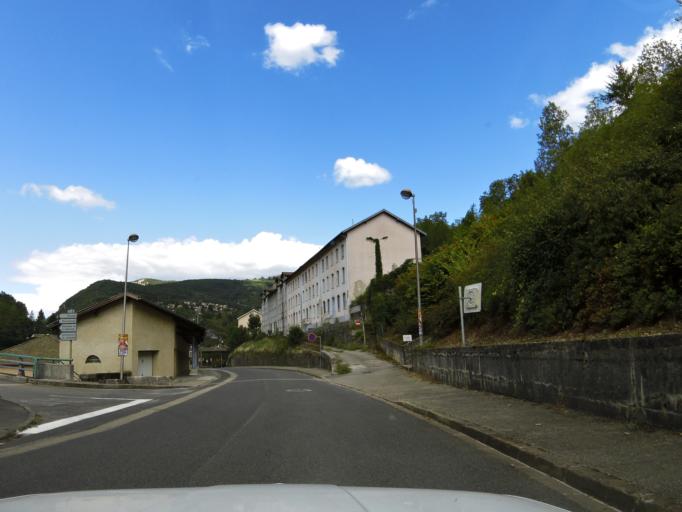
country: FR
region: Rhone-Alpes
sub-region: Departement de l'Ain
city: Tenay
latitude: 45.9136
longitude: 5.5103
